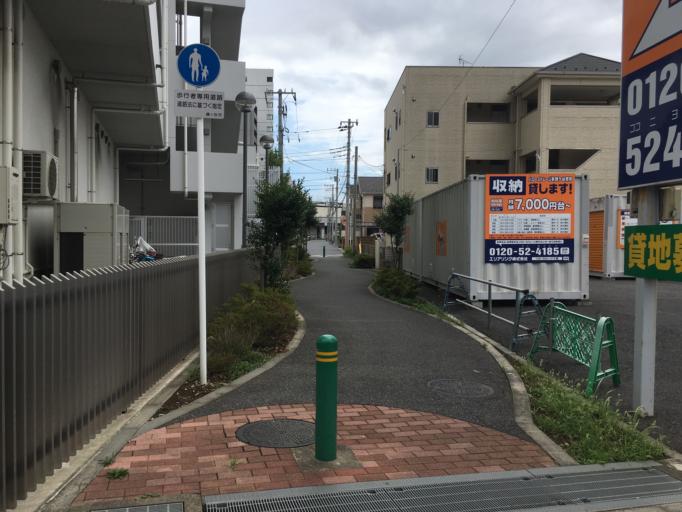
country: JP
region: Chiba
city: Shiroi
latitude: 35.7814
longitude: 139.9987
